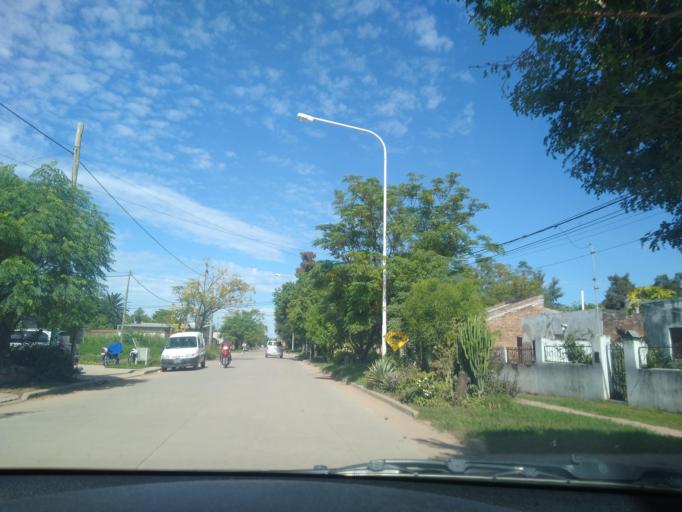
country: AR
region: Chaco
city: Presidencia Roque Saenz Pena
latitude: -26.7765
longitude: -60.4249
